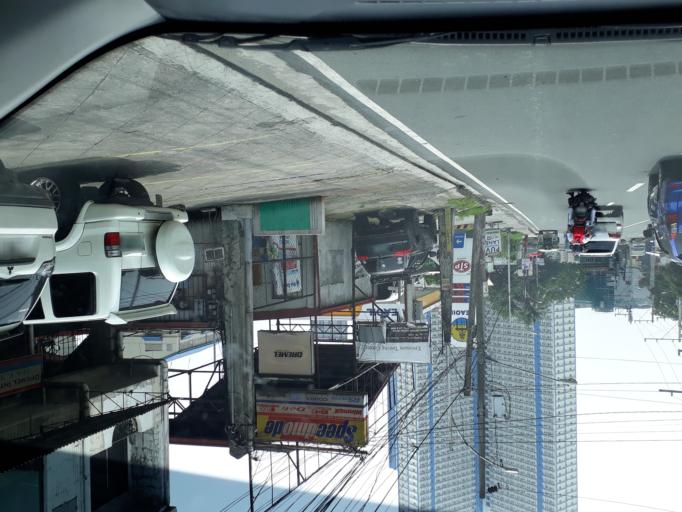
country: PH
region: Metro Manila
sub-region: City of Manila
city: Manila
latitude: 14.6180
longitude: 121.0047
